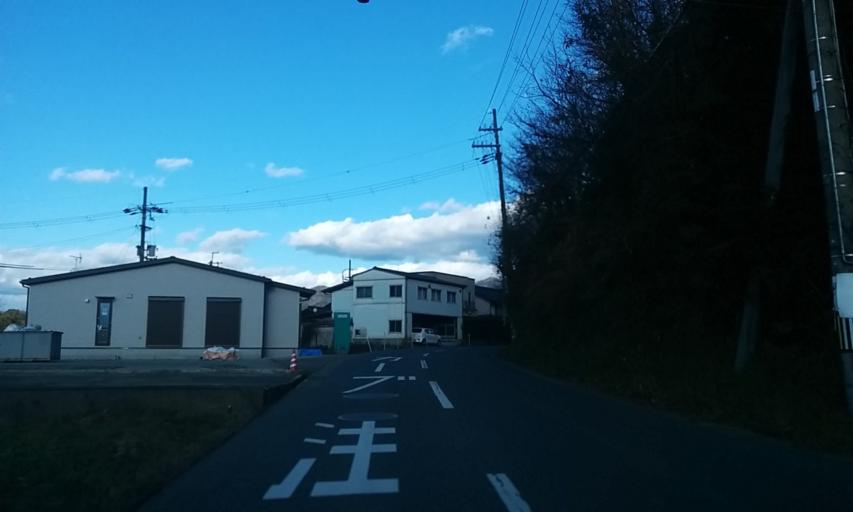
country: JP
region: Kyoto
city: Fukuchiyama
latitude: 35.3051
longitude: 135.1016
